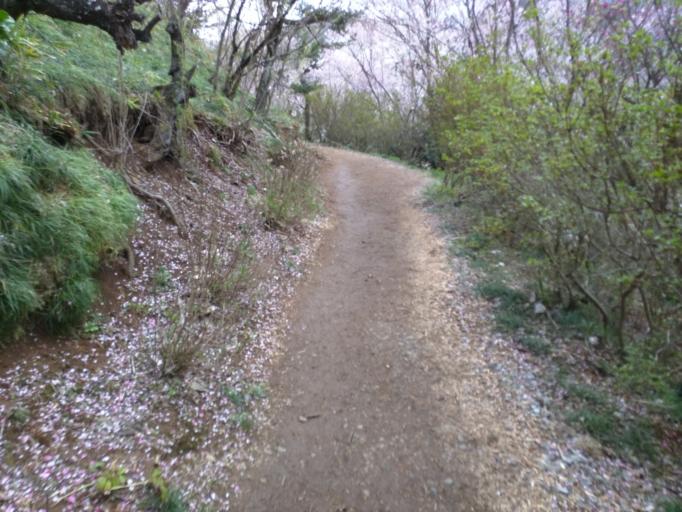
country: JP
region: Fukushima
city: Fukushima-shi
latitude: 37.7389
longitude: 140.4949
